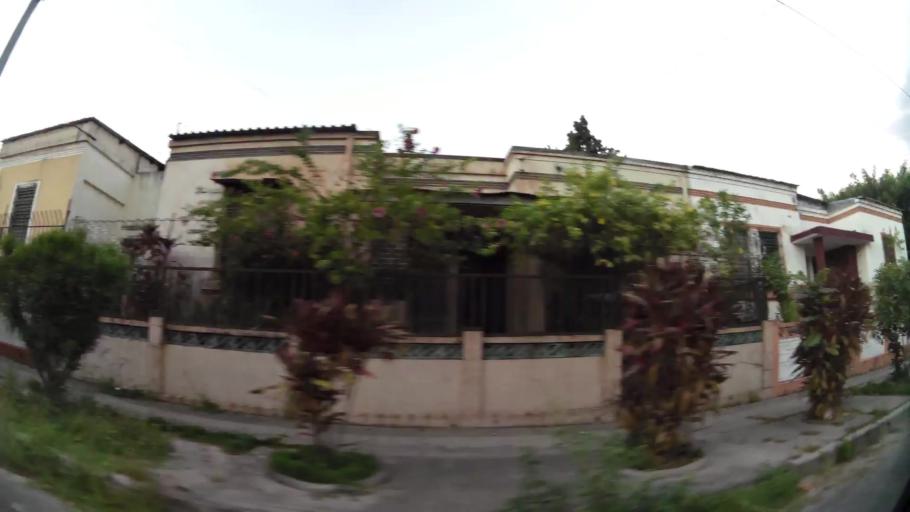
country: SV
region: San Salvador
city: San Salvador
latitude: 13.7062
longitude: -89.1850
